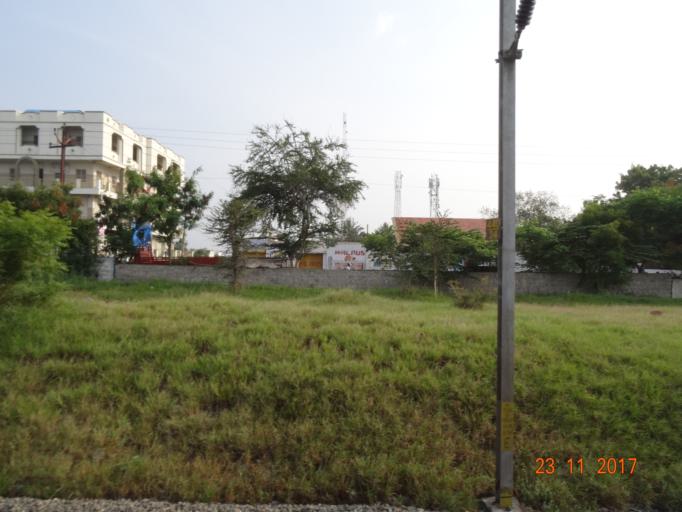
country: IN
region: Tamil Nadu
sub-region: Tiruppur
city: Tiruppur
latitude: 11.1127
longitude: 77.3555
